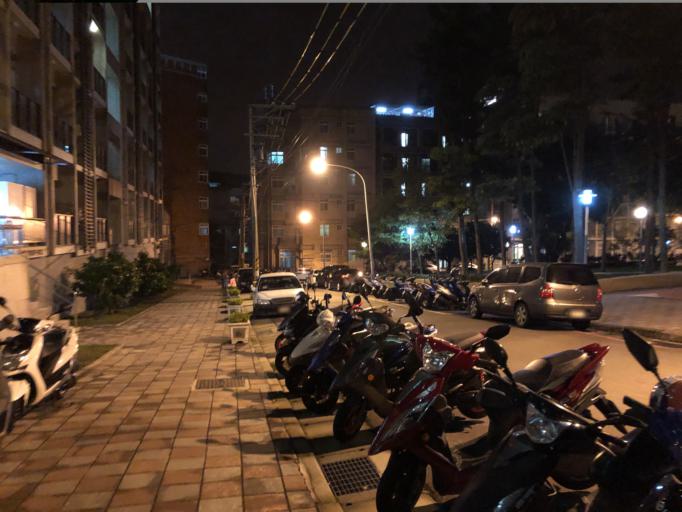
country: TW
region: Taiwan
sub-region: Taoyuan
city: Taoyuan
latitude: 24.9895
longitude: 121.3421
